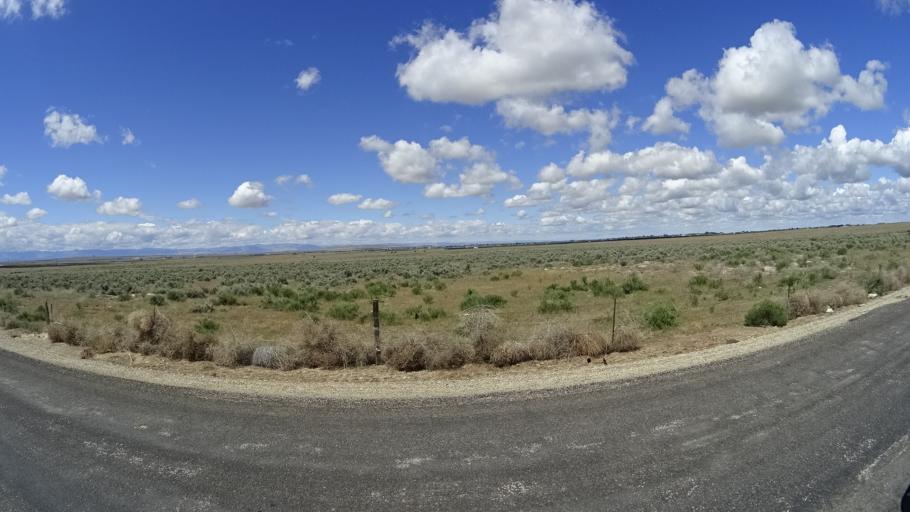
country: US
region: Idaho
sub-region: Ada County
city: Kuna
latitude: 43.4646
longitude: -116.2744
